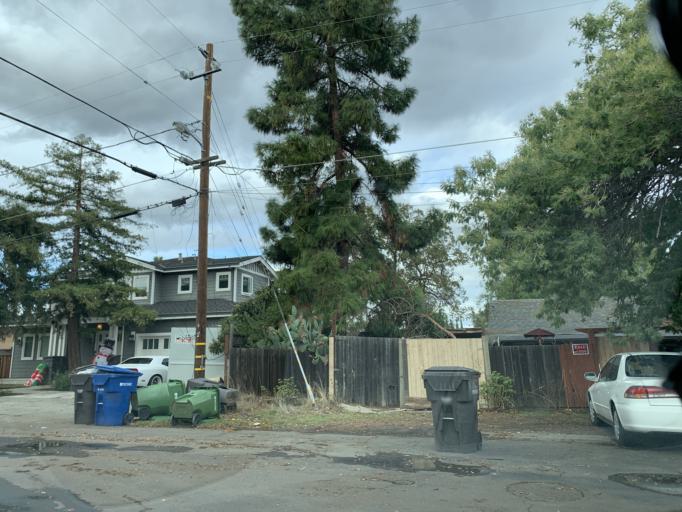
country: US
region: California
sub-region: Santa Clara County
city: Campbell
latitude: 37.2767
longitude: -121.9686
